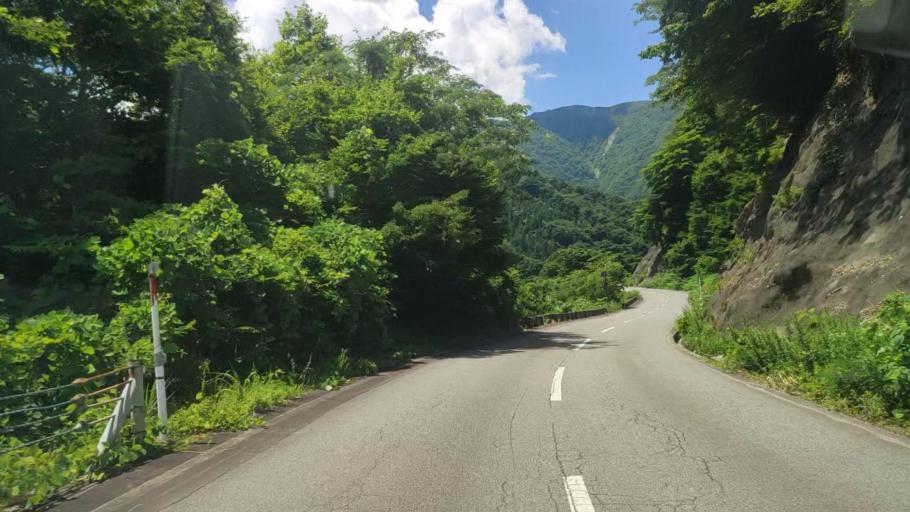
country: JP
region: Fukui
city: Ono
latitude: 35.8958
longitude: 136.5218
